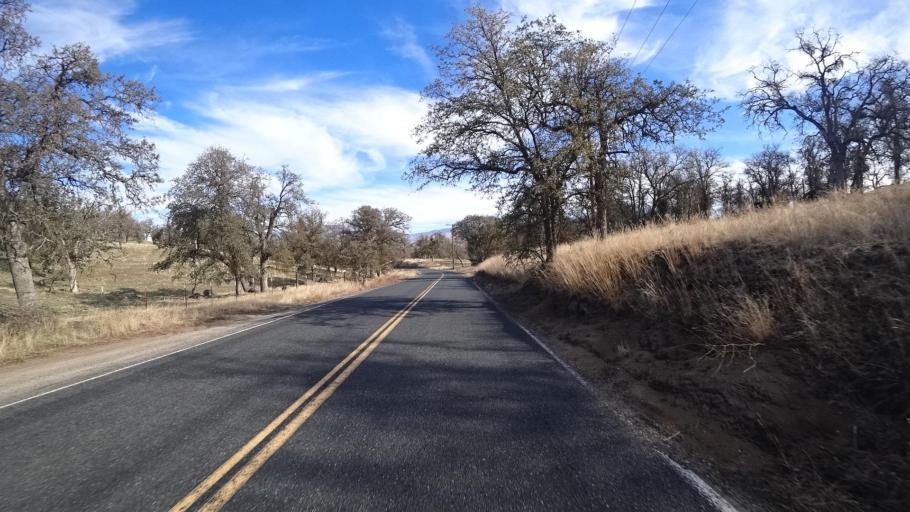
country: US
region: California
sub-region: Kern County
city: Alta Sierra
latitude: 35.6550
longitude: -118.7602
